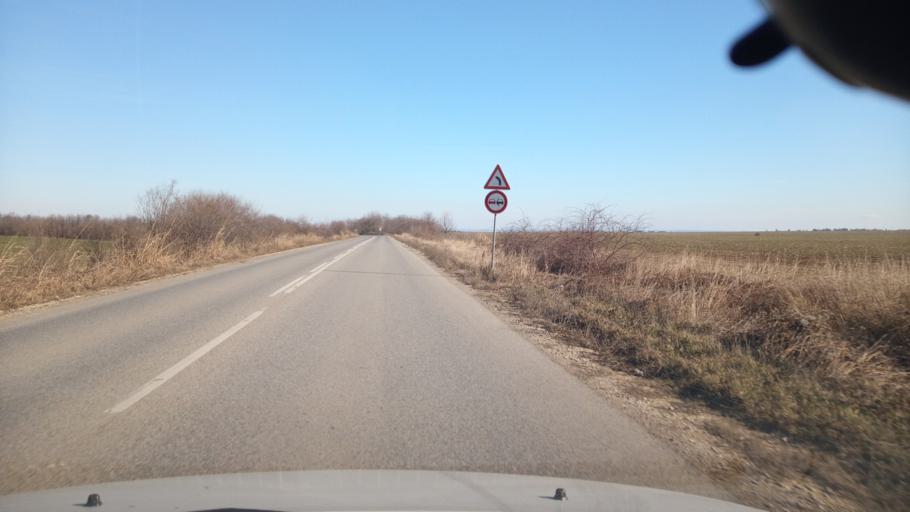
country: BG
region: Pleven
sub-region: Obshtina Pleven
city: Pleven
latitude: 43.4279
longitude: 24.7157
